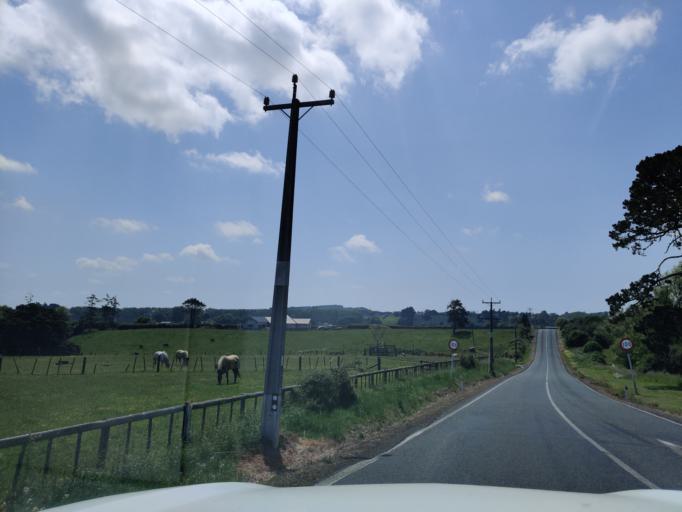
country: NZ
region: Auckland
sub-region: Auckland
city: Pukekohe East
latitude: -37.2147
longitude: 174.9363
